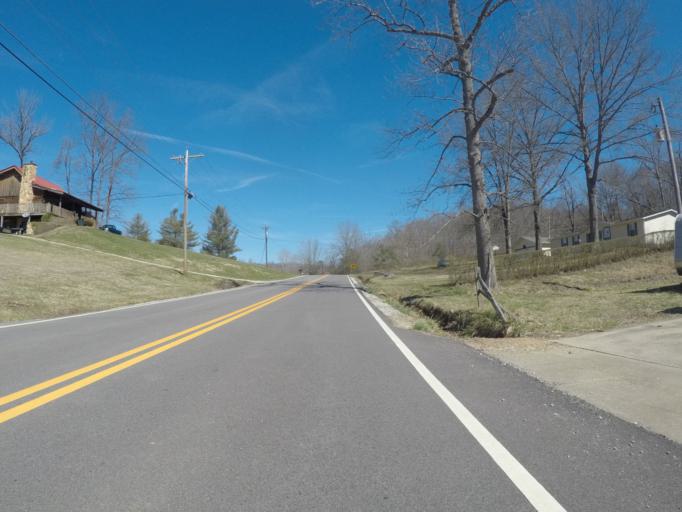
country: US
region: Ohio
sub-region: Lawrence County
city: Burlington
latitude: 38.4546
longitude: -82.5385
